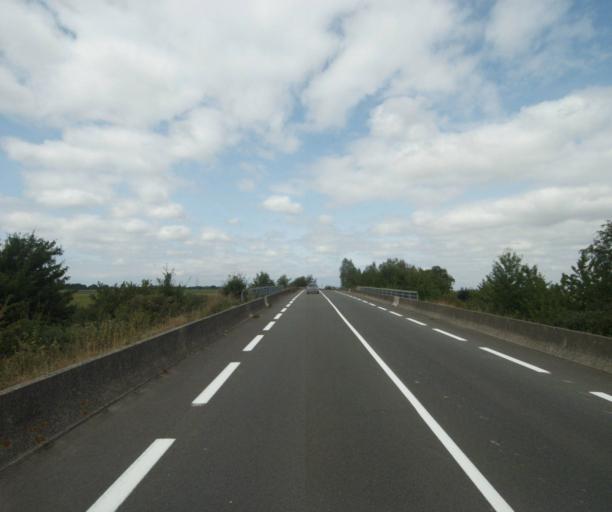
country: FR
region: Nord-Pas-de-Calais
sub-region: Departement du Nord
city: Cysoing
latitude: 50.5764
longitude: 3.2179
